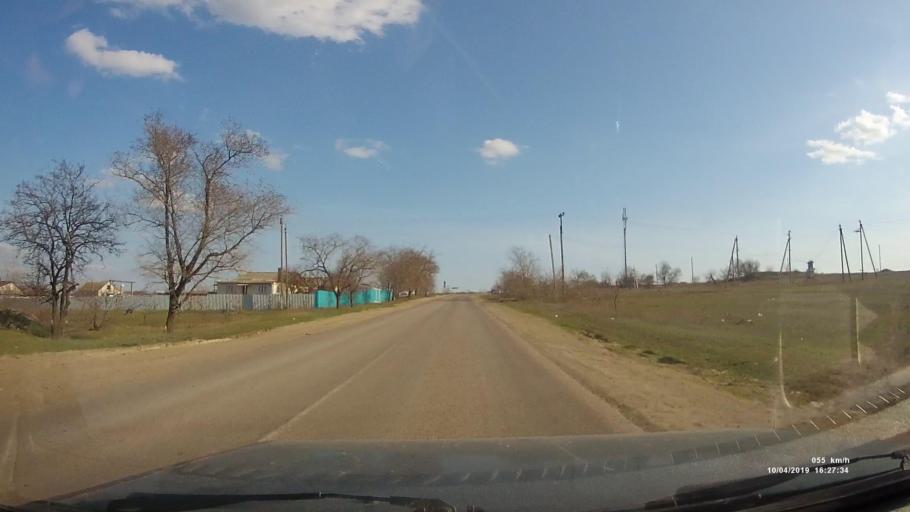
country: RU
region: Rostov
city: Staraya Stanitsa
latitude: 48.2832
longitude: 40.3433
